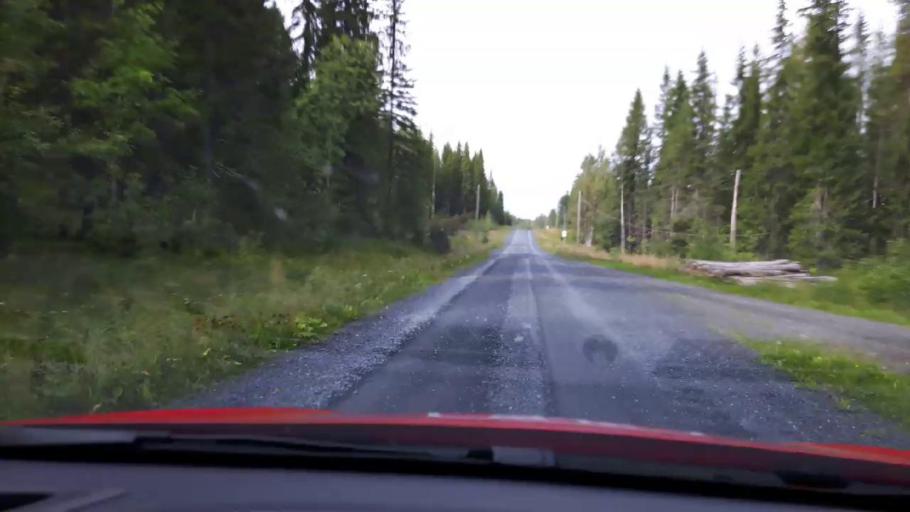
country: SE
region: Jaemtland
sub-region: Krokoms Kommun
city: Valla
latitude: 63.2703
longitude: 13.7602
